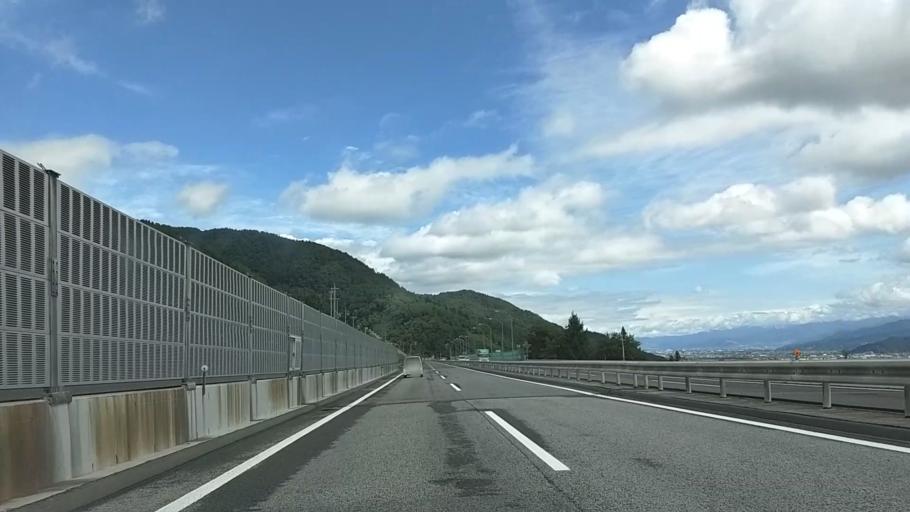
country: JP
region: Nagano
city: Nagano-shi
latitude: 36.5210
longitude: 138.0755
